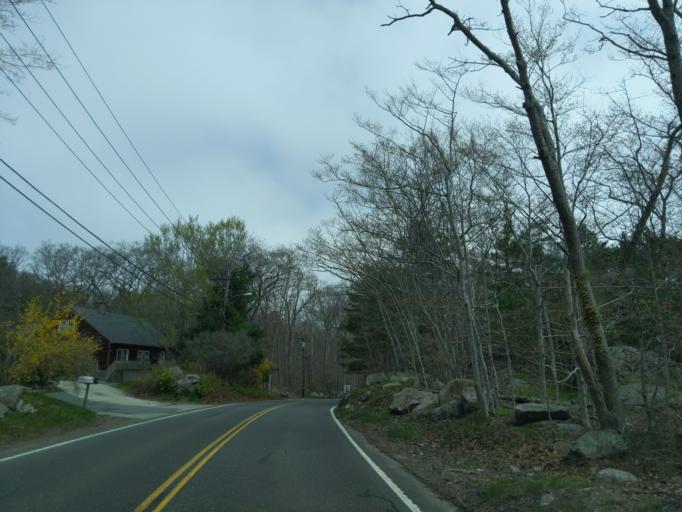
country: US
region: Massachusetts
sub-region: Essex County
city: Rockport
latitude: 42.6305
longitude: -70.6225
